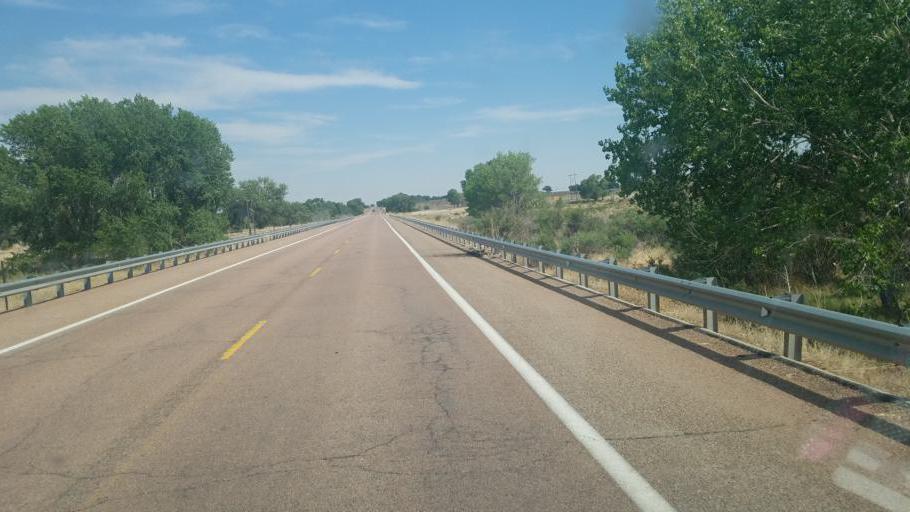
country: US
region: Colorado
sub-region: Pueblo County
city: Pueblo
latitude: 38.2436
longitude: -104.3422
